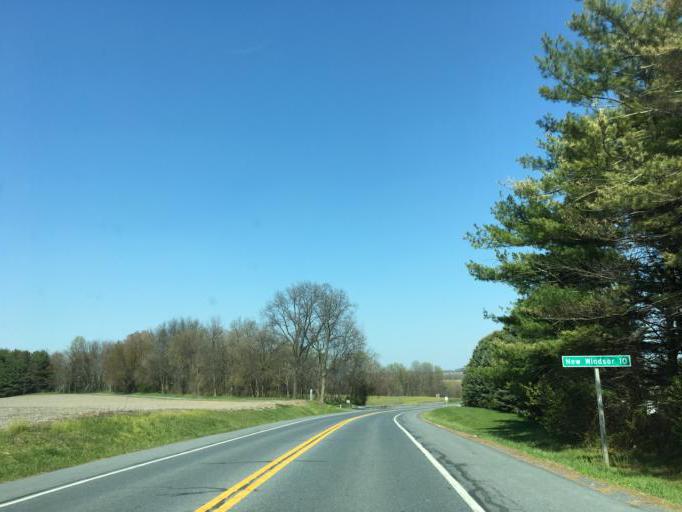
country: US
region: Maryland
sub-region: Frederick County
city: Linganore
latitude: 39.4851
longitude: -77.2315
